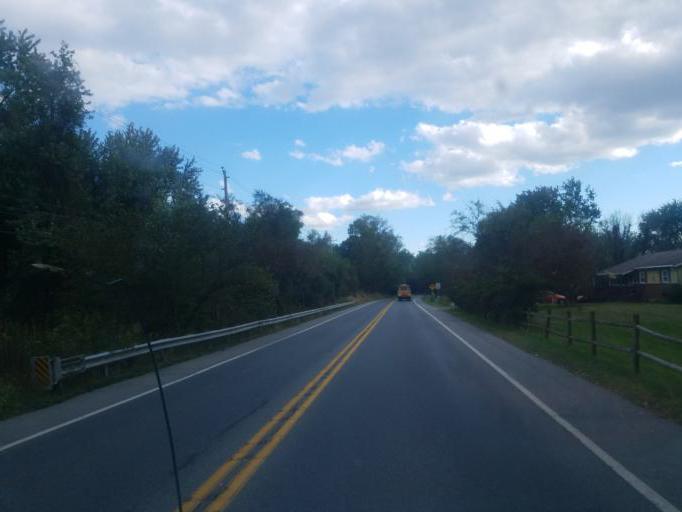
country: US
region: Pennsylvania
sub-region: Dauphin County
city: Middletown
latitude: 40.1675
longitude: -76.7204
